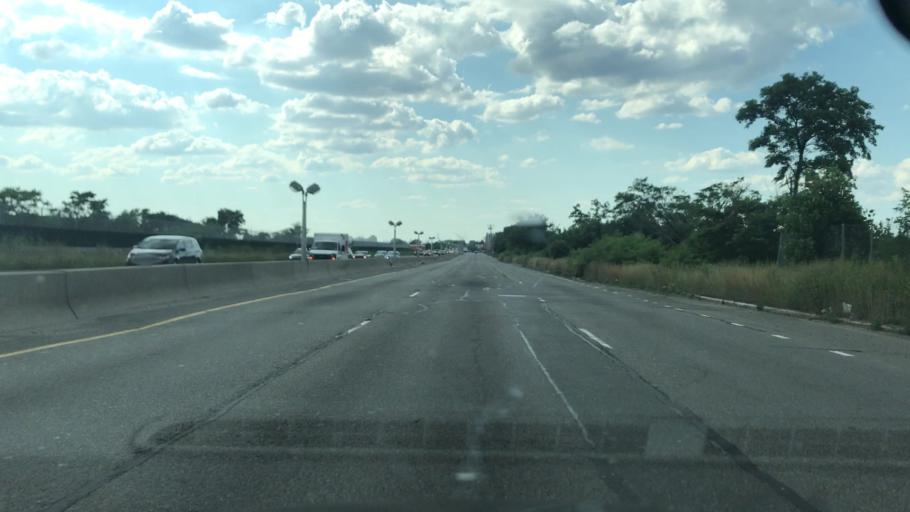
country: US
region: New York
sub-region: Nassau County
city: Inwood
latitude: 40.6525
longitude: -73.7606
